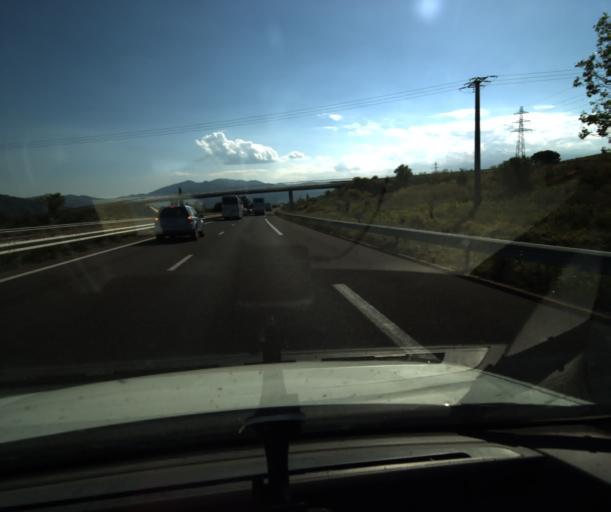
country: FR
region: Languedoc-Roussillon
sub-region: Departement des Pyrenees-Orientales
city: el Volo
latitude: 42.5420
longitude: 2.8455
